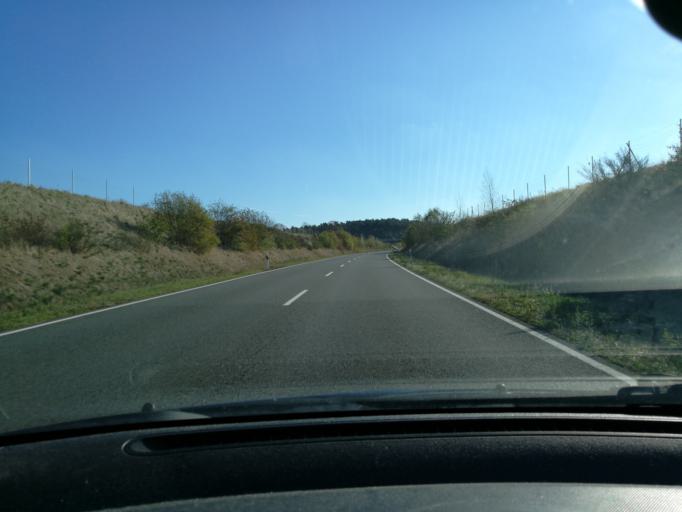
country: DE
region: Lower Saxony
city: Dahlem
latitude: 53.1906
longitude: 10.7570
